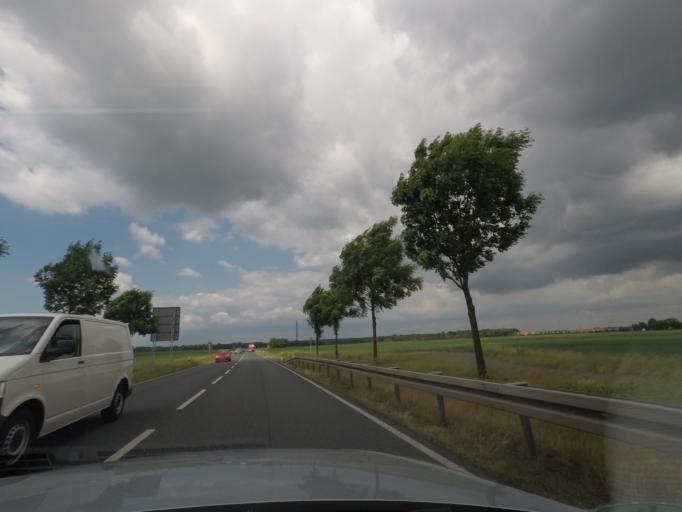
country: DE
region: Saxony
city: Markranstadt
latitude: 51.2770
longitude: 12.2620
